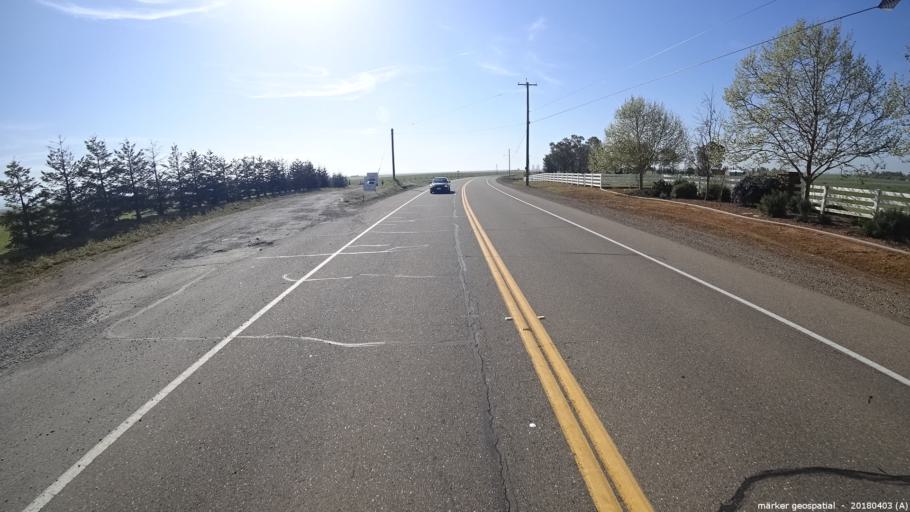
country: US
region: California
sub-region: Sacramento County
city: Clay
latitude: 38.4142
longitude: -121.1770
